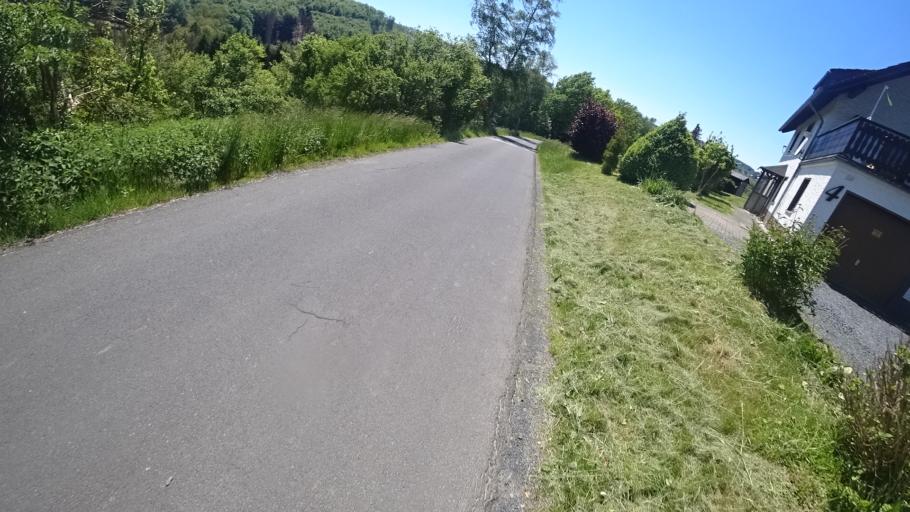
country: DE
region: Rheinland-Pfalz
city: Steineroth
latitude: 50.7485
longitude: 7.8488
